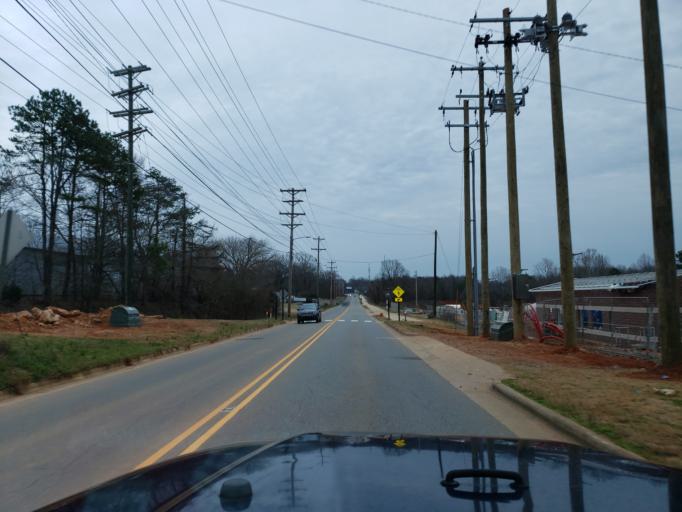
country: US
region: North Carolina
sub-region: Cleveland County
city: Shelby
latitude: 35.3032
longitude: -81.5543
